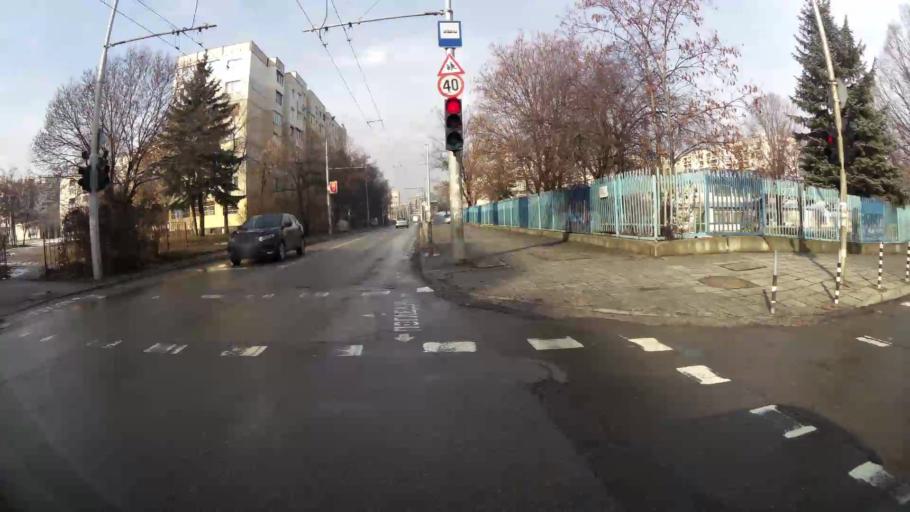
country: BG
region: Sofia-Capital
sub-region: Stolichna Obshtina
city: Sofia
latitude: 42.7211
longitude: 23.2648
